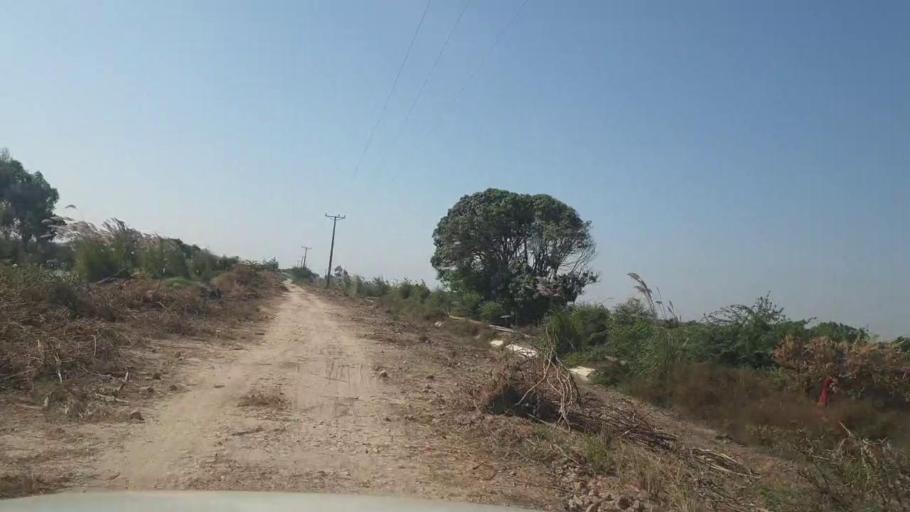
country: PK
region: Sindh
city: Chuhar Jamali
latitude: 24.4232
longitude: 67.8167
